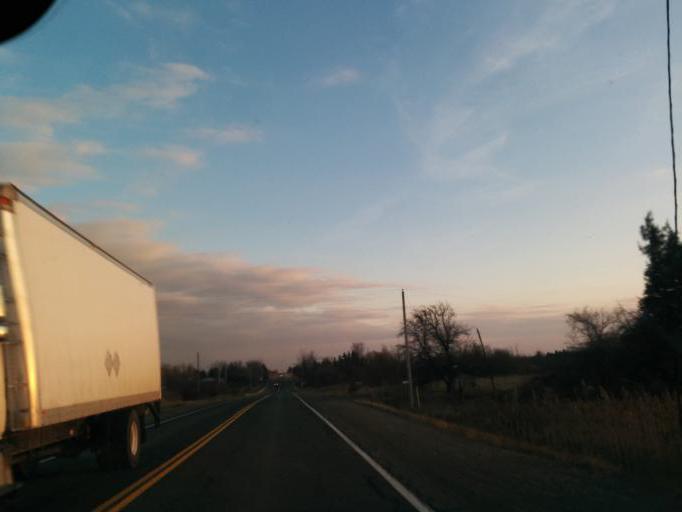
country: CA
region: Ontario
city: Brampton
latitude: 43.8541
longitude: -79.7743
